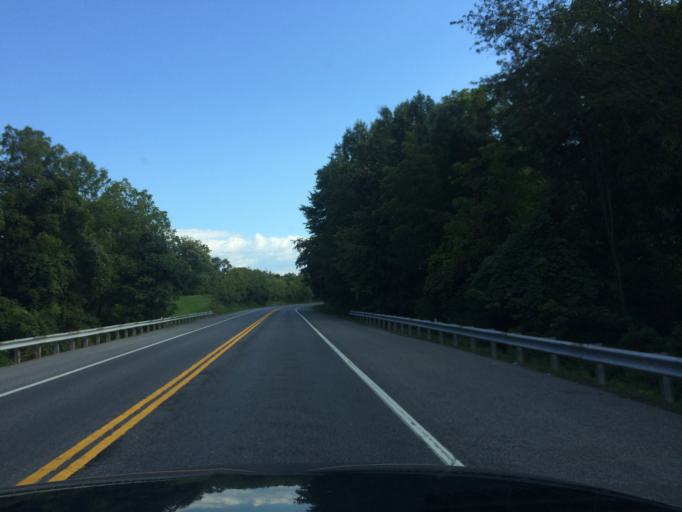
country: US
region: Maryland
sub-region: Carroll County
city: Eldersburg
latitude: 39.4495
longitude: -76.9982
